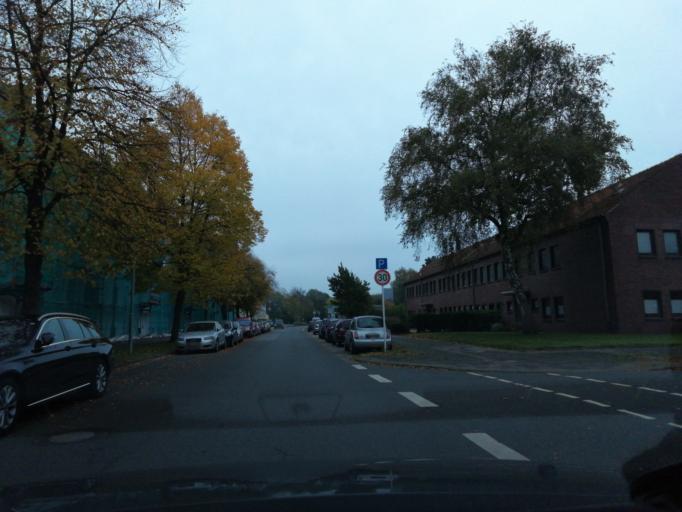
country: DE
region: Lower Saxony
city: Wilhelmshaven
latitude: 53.5251
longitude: 8.1346
